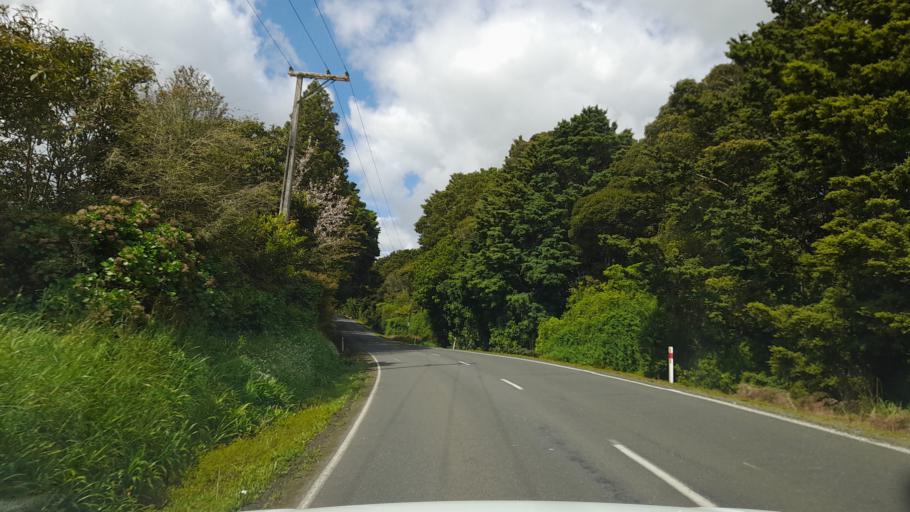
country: NZ
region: Northland
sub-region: Whangarei
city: Maungatapere
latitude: -35.6590
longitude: 174.1672
